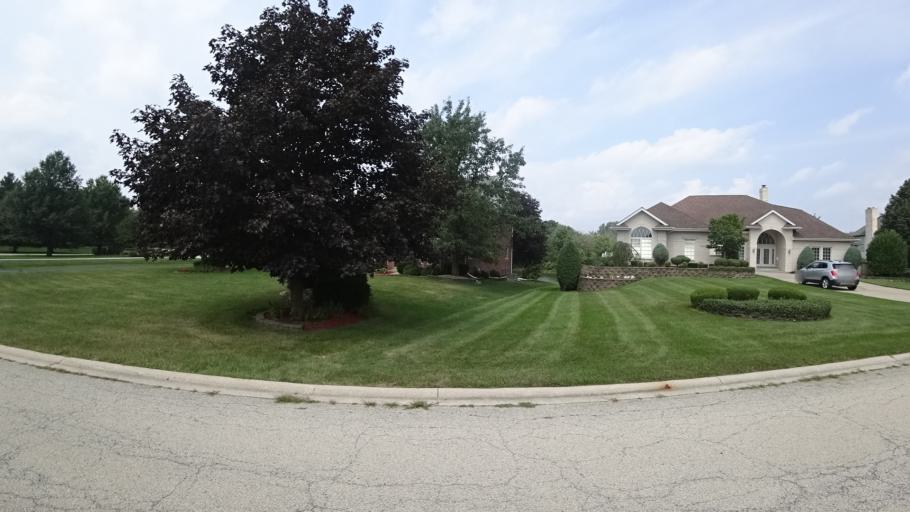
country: US
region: Illinois
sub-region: Will County
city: Goodings Grove
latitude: 41.6191
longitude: -87.9122
